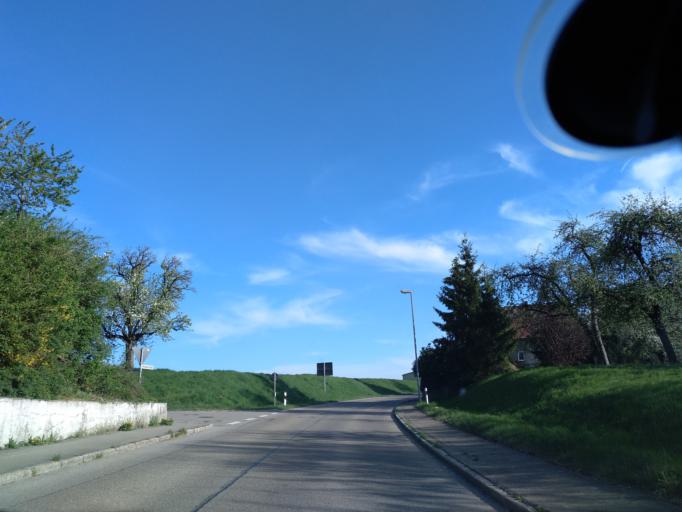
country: DE
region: Baden-Wuerttemberg
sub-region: Regierungsbezirk Stuttgart
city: Langenburg
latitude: 49.2250
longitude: 9.8479
